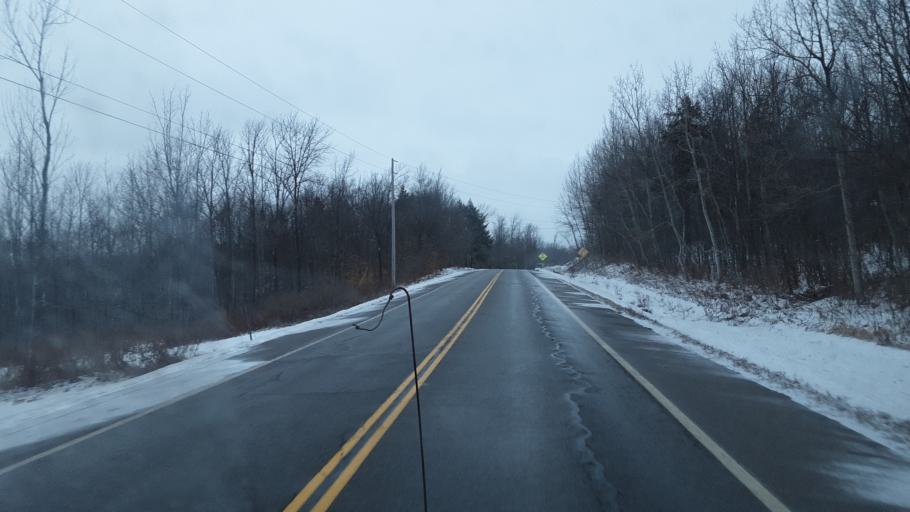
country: US
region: Pennsylvania
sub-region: Tioga County
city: Westfield
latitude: 42.0974
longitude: -77.5376
